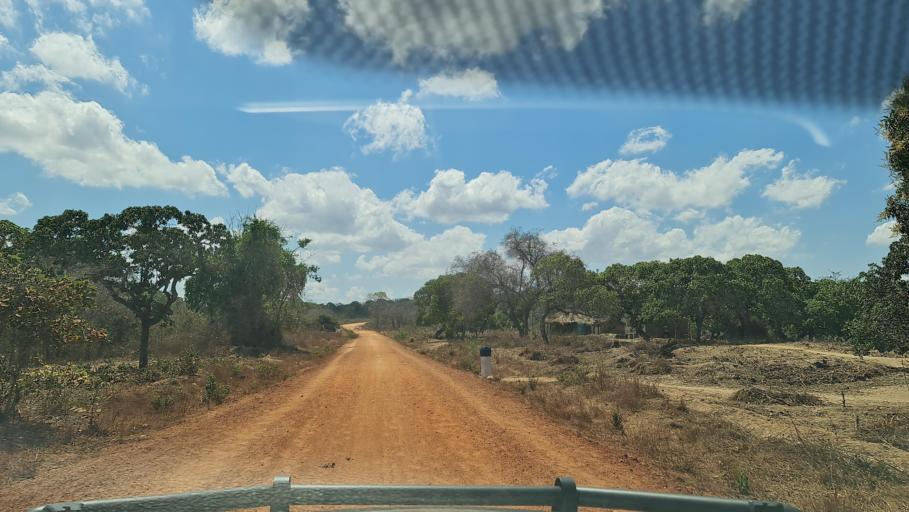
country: MZ
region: Nampula
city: Nacala
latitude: -14.1691
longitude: 40.2514
